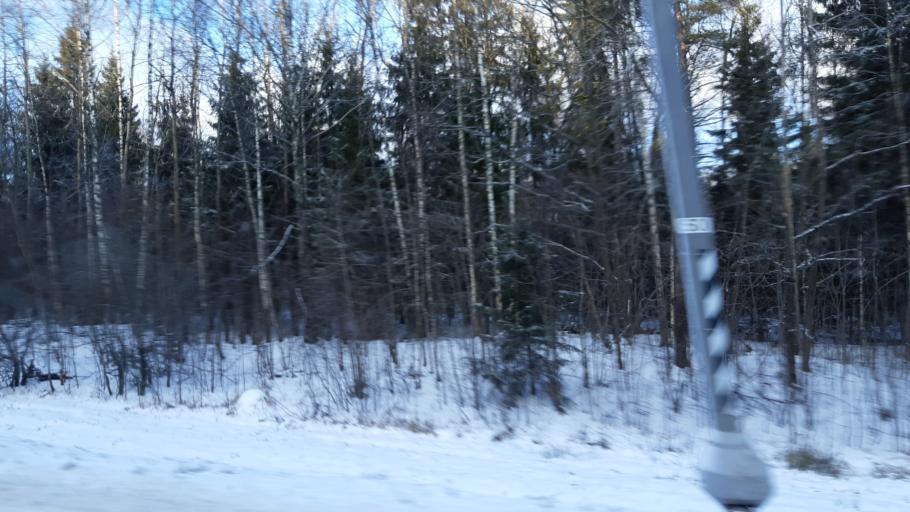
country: RU
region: Moskovskaya
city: Svatkovo
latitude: 56.3050
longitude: 38.3348
